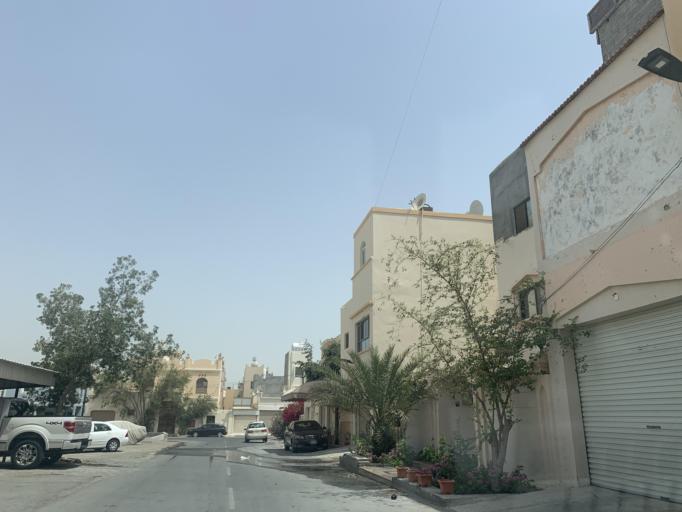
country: BH
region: Central Governorate
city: Madinat Hamad
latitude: 26.1496
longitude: 50.5180
